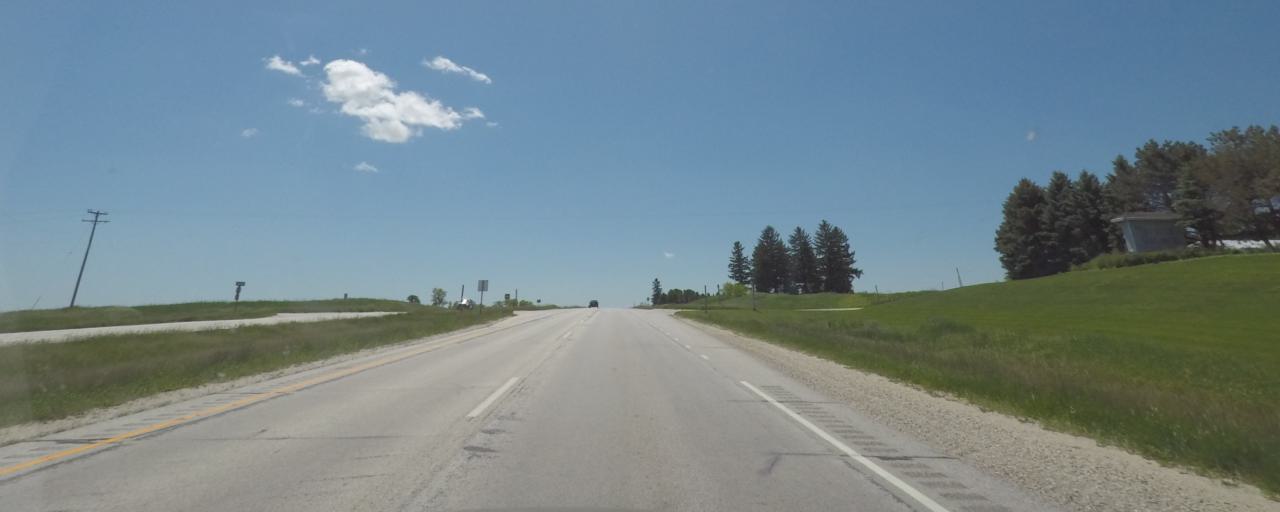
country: US
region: Wisconsin
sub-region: Sheboygan County
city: Plymouth
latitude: 43.7191
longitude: -87.9410
